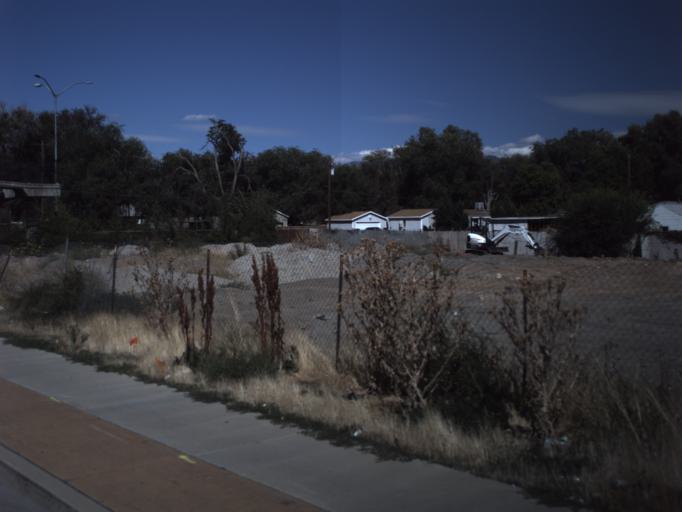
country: US
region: Utah
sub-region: Salt Lake County
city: Taylorsville
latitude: 40.7127
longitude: -111.9388
